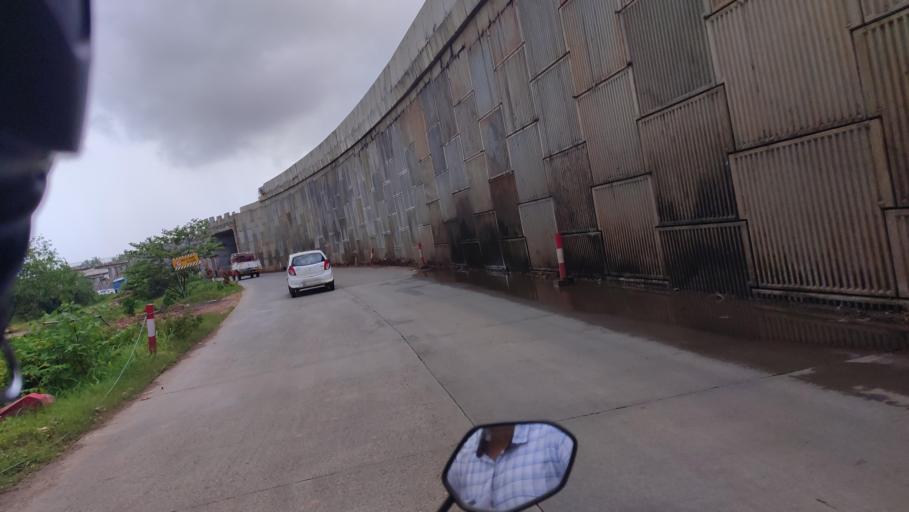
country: IN
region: Kerala
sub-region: Kasaragod District
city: Nileshwar
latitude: 12.2424
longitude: 75.1479
